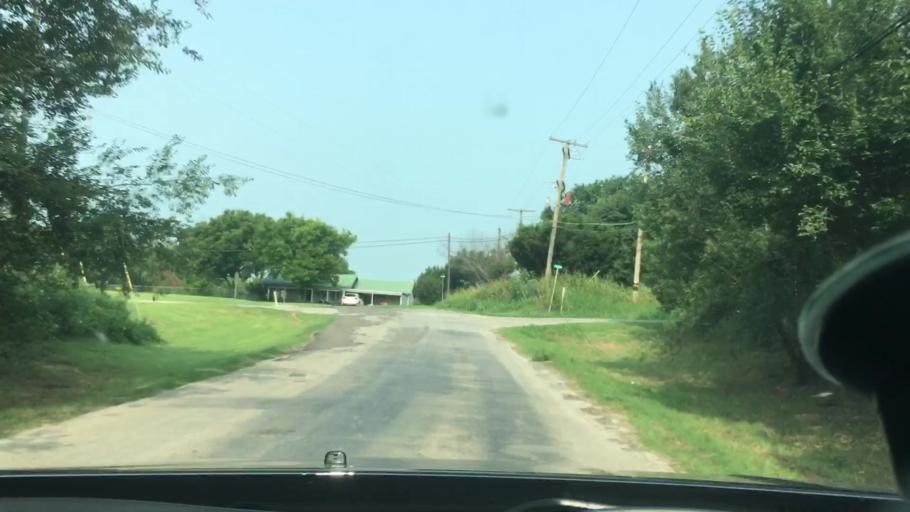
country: US
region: Oklahoma
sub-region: Garvin County
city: Lindsay
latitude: 34.8125
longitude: -97.6057
